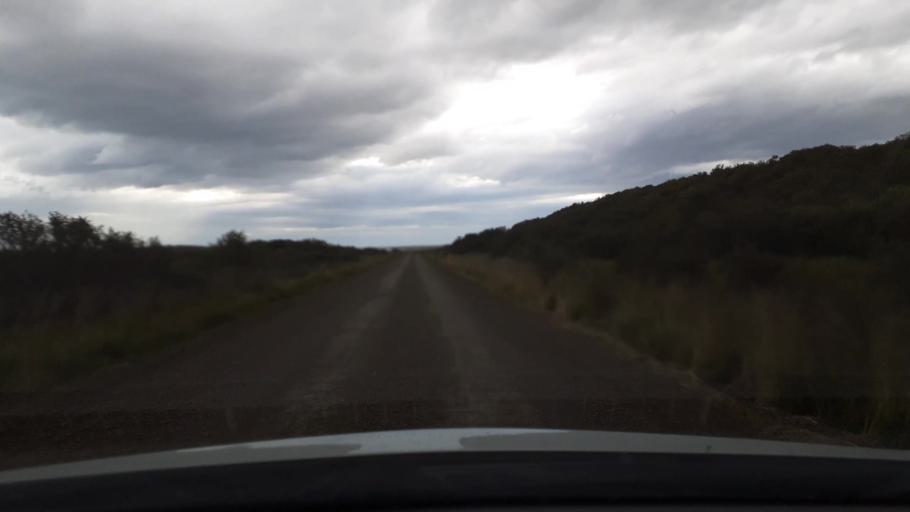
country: IS
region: West
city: Borgarnes
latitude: 64.6036
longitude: -21.9691
